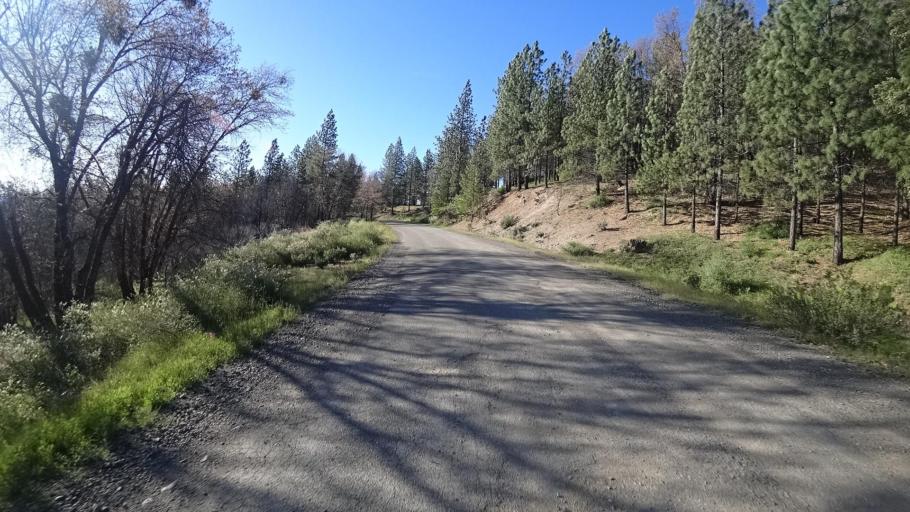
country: US
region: California
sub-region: Lake County
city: Upper Lake
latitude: 39.3138
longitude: -122.9467
